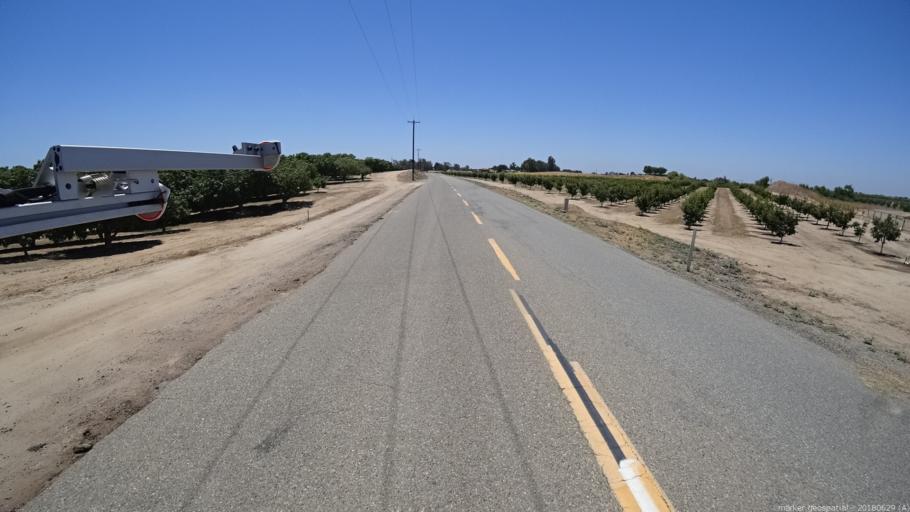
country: US
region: California
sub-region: Madera County
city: Parksdale
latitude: 37.0101
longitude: -119.9712
